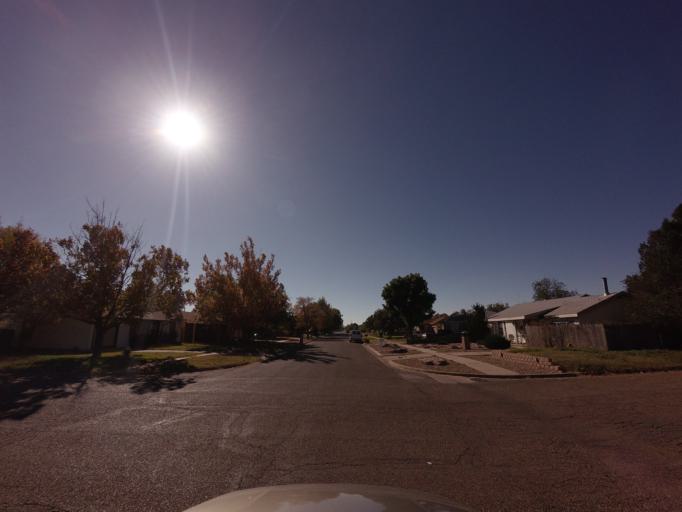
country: US
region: New Mexico
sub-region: Curry County
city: Clovis
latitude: 34.4286
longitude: -103.1990
